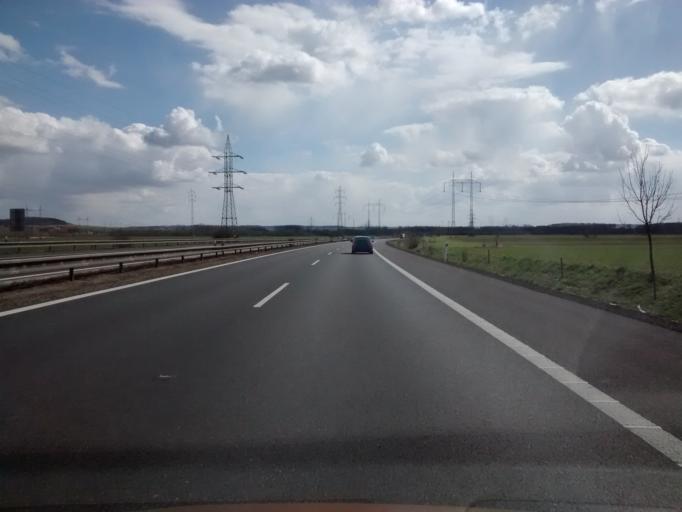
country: CZ
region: Central Bohemia
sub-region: Okres Melnik
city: Veltrusy
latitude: 50.2889
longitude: 14.3505
